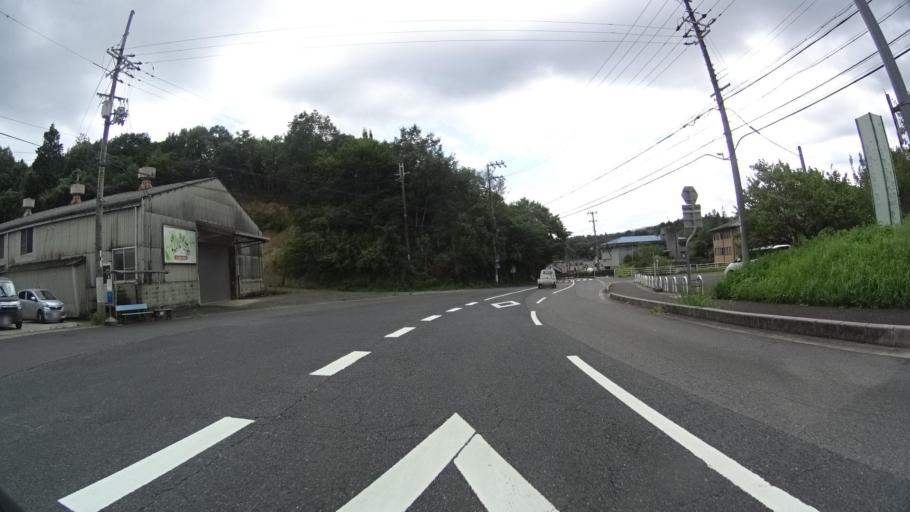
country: JP
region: Mie
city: Ueno-ebisumachi
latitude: 34.7108
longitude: 136.0454
